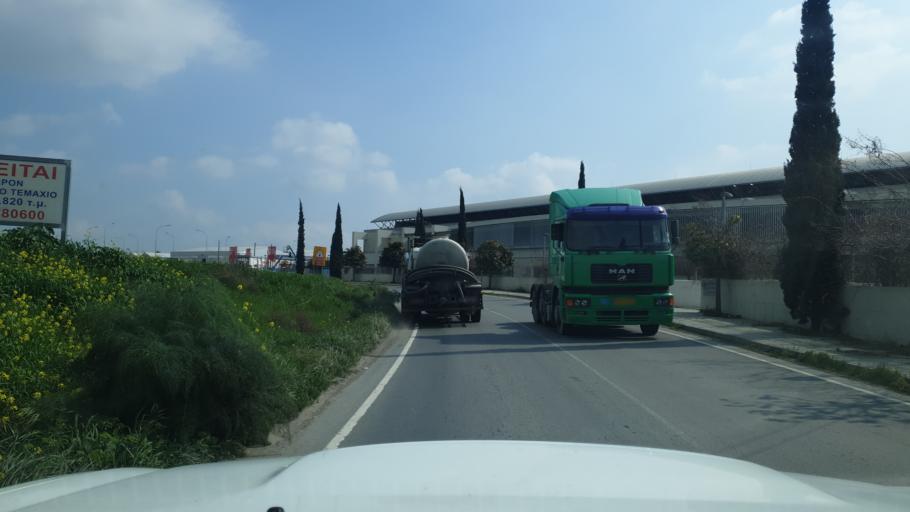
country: CY
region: Lefkosia
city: Dali
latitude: 35.0560
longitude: 33.3865
